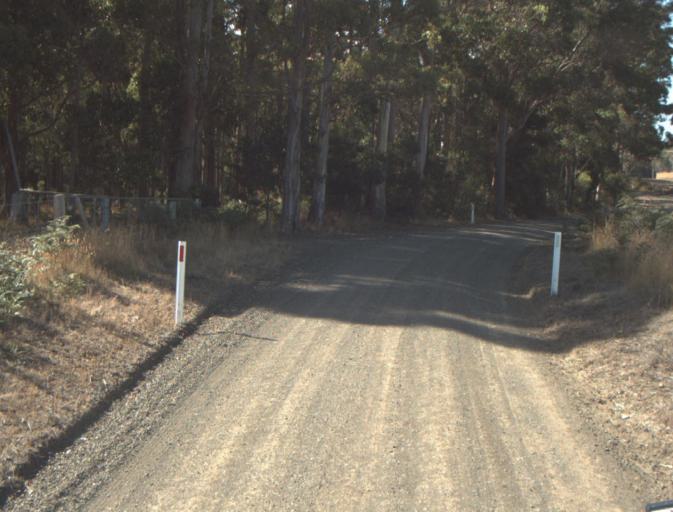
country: AU
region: Tasmania
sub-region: Dorset
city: Bridport
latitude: -41.1566
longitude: 147.2350
